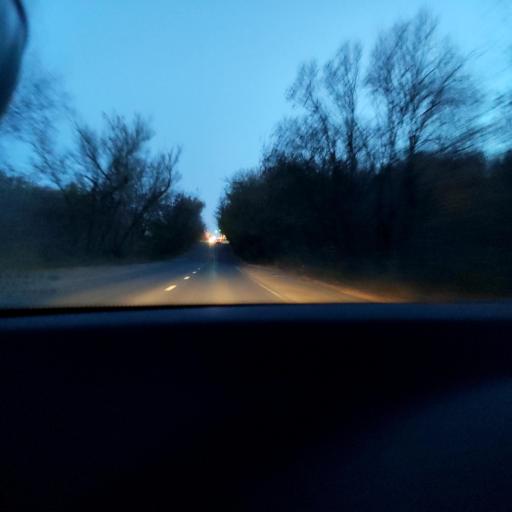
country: RU
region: Samara
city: Petra-Dubrava
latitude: 53.3111
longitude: 50.2750
